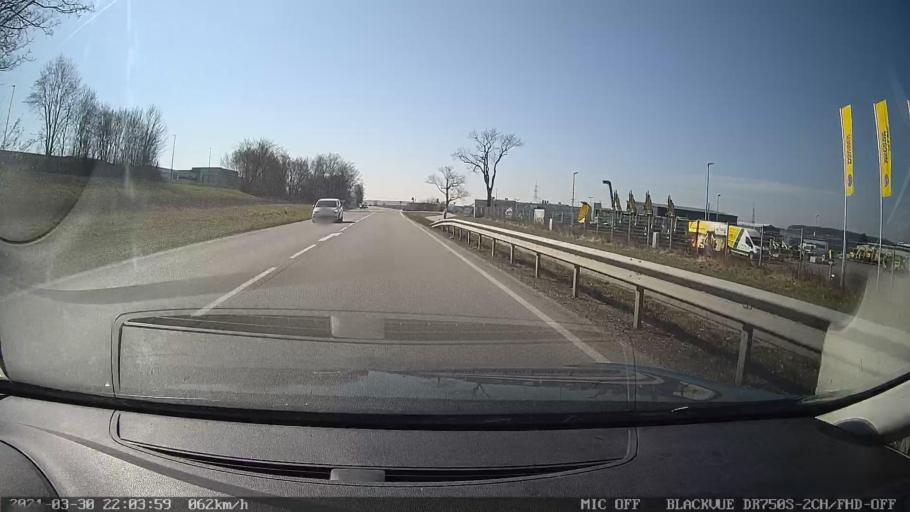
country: DE
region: Bavaria
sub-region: Upper Palatinate
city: Regenstauf
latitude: 49.1096
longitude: 12.1247
